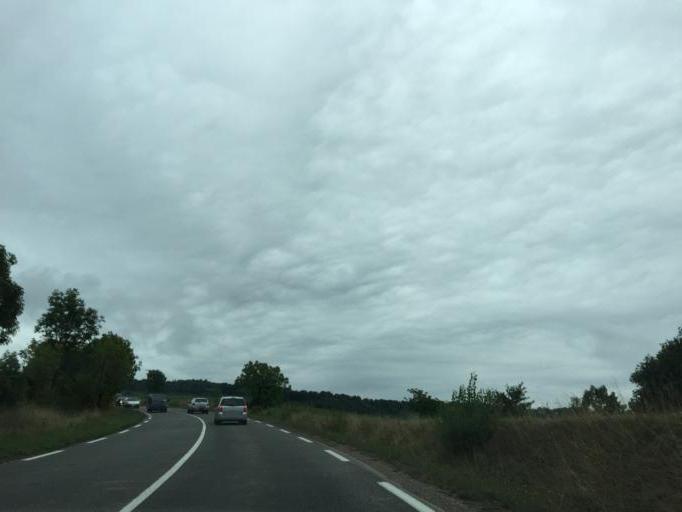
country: FR
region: Midi-Pyrenees
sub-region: Departement de l'Aveyron
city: Espalion
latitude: 44.5112
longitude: 2.7345
